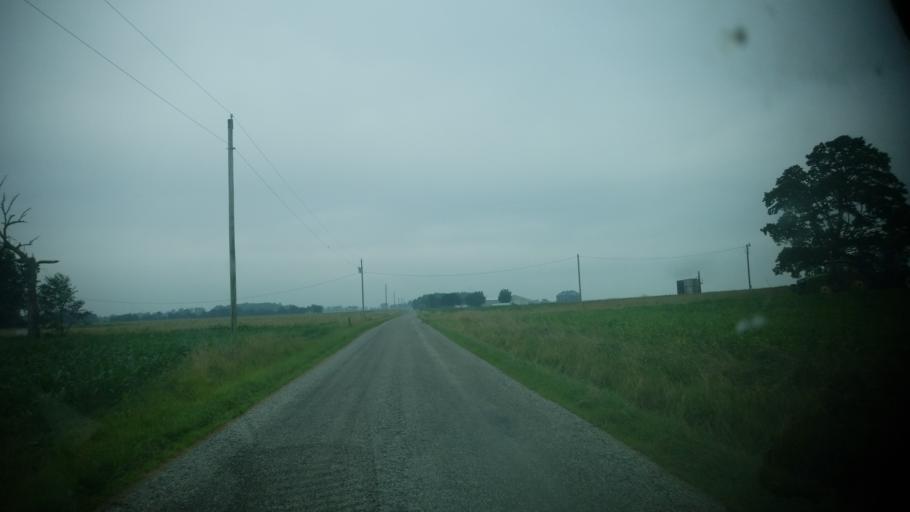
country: US
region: Illinois
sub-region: Clay County
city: Flora
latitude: 38.5737
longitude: -88.4103
